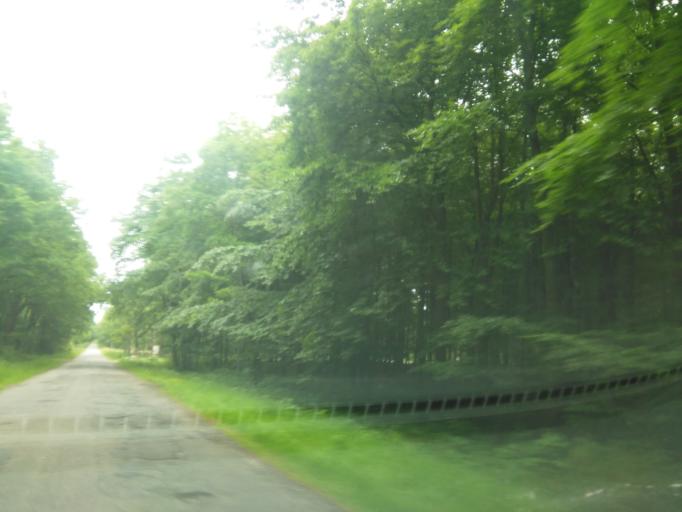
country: DK
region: Capital Region
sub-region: Bornholm Kommune
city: Akirkeby
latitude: 55.1128
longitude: 14.9380
